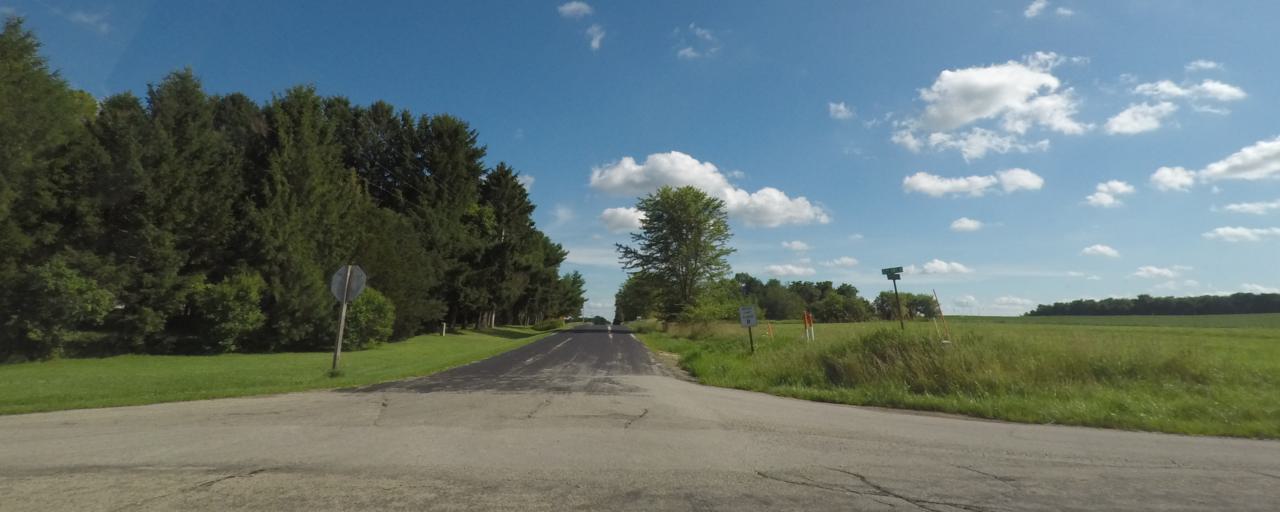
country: US
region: Wisconsin
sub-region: Rock County
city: Edgerton
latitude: 42.8616
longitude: -89.1320
